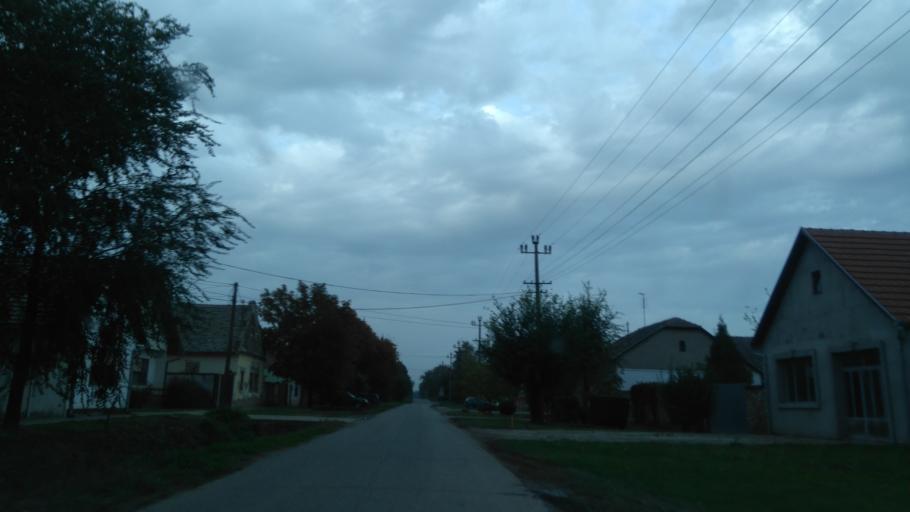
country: RS
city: Mol
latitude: 45.7620
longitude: 20.1365
